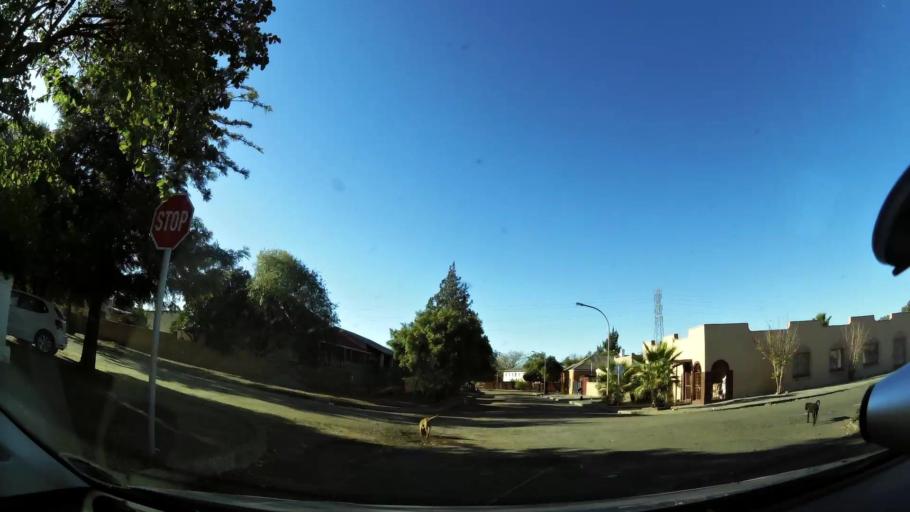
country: ZA
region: Northern Cape
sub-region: Frances Baard District Municipality
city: Kimberley
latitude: -28.7549
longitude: 24.7875
